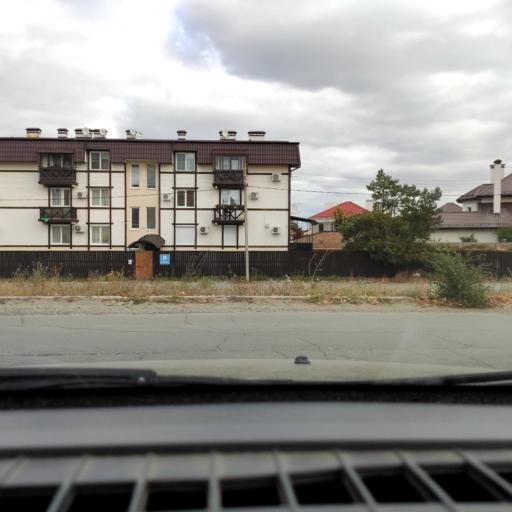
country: RU
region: Samara
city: Tol'yatti
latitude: 53.5392
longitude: 49.3634
